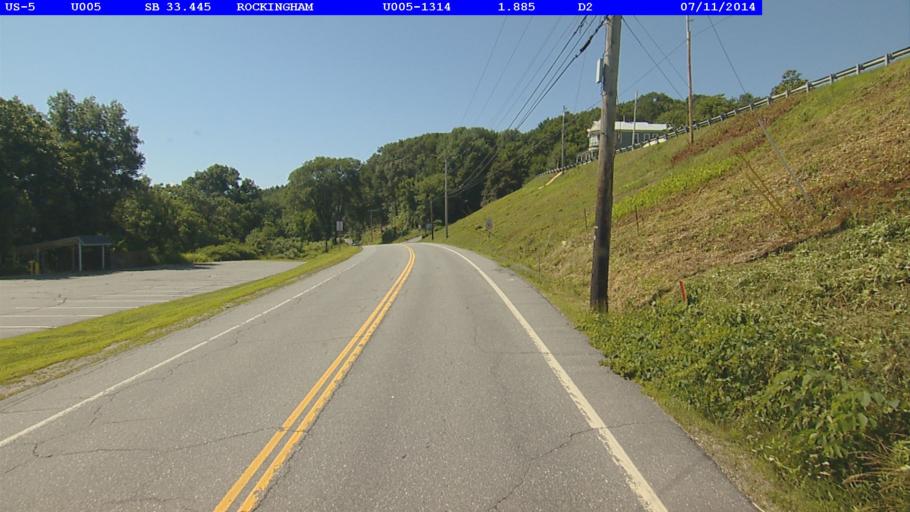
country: US
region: Vermont
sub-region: Windham County
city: Bellows Falls
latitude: 43.1484
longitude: -72.4589
